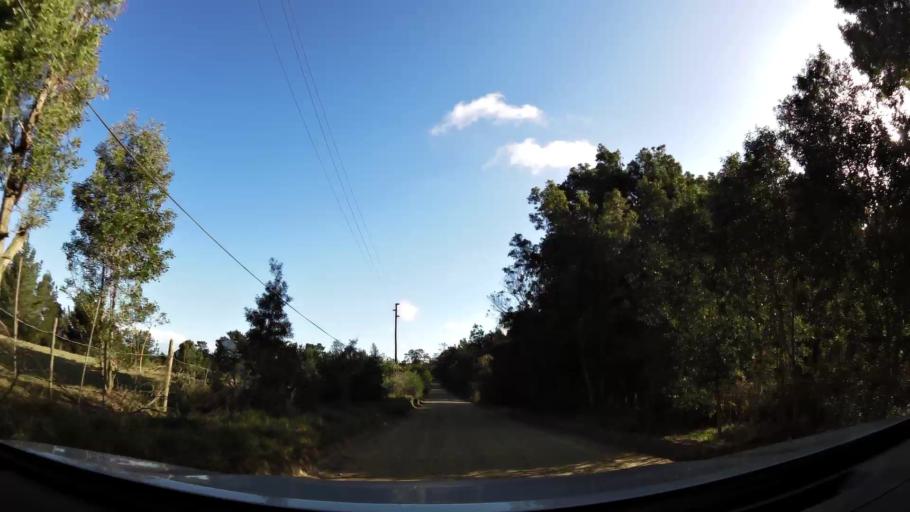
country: ZA
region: Western Cape
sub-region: Eden District Municipality
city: George
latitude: -33.9800
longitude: 22.5722
